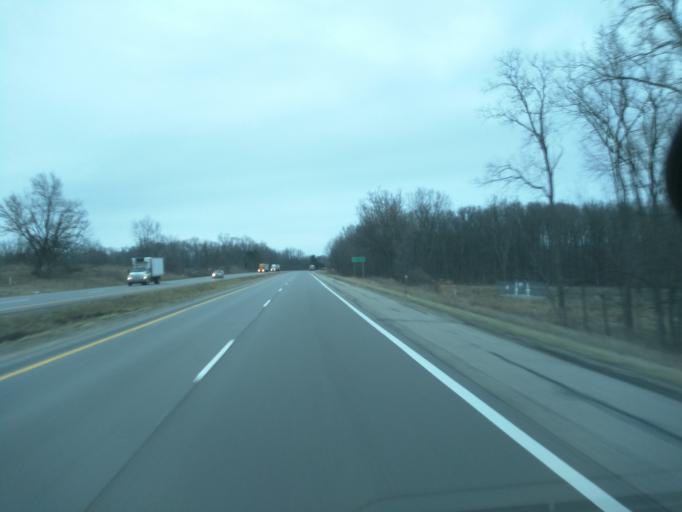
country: US
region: Michigan
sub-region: Ingham County
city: Leslie
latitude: 42.4216
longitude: -84.4332
